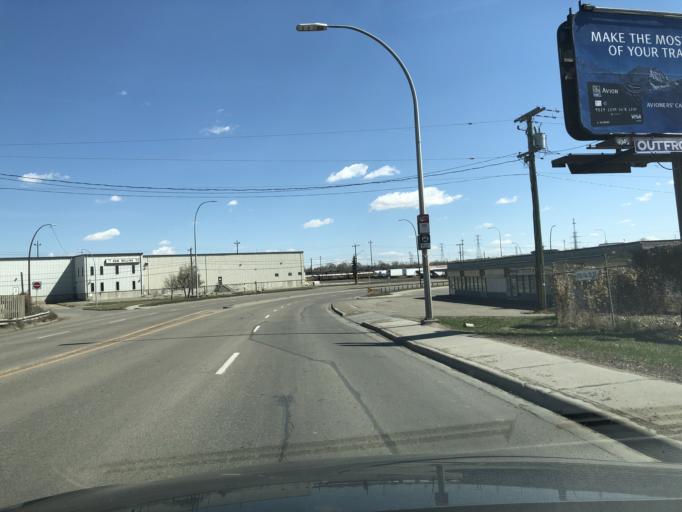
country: CA
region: Alberta
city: Calgary
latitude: 51.0185
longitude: -114.0203
